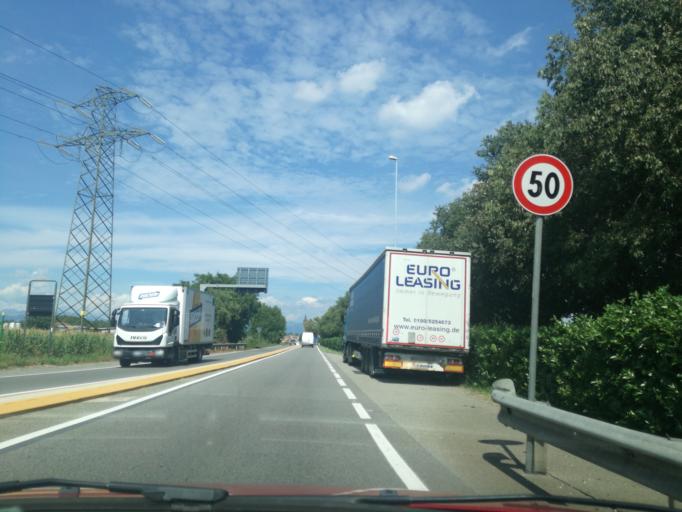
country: IT
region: Lombardy
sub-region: Citta metropolitana di Milano
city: Trezzo sull'Adda
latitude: 45.6001
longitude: 9.5073
